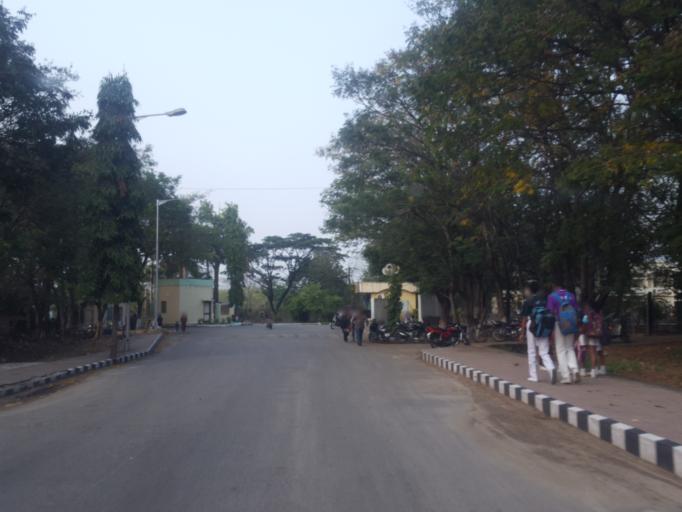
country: IN
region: Telangana
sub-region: Rangareddi
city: Singapur
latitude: 17.4698
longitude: 78.1630
